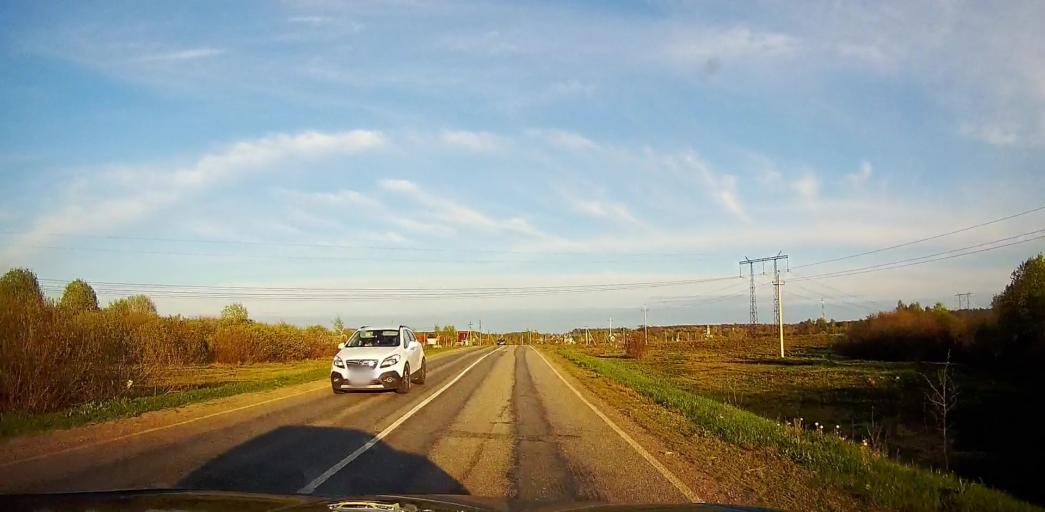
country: RU
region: Moskovskaya
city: Meshcherino
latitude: 55.2633
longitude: 38.2604
